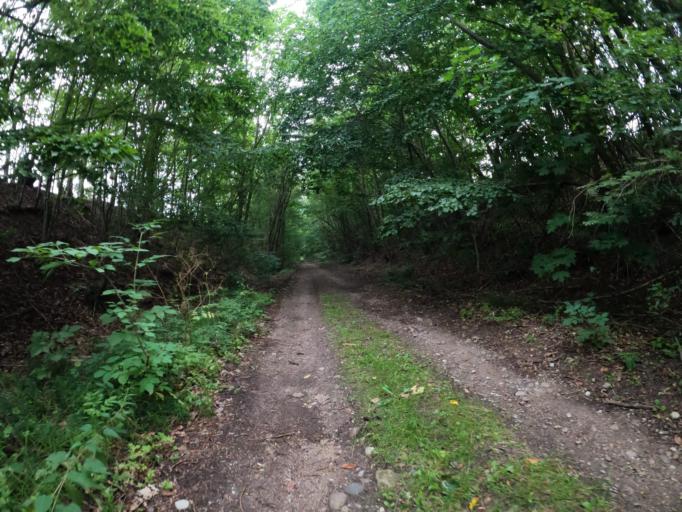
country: PL
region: West Pomeranian Voivodeship
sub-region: Powiat szczecinecki
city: Grzmiaca
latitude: 53.8812
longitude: 16.4762
